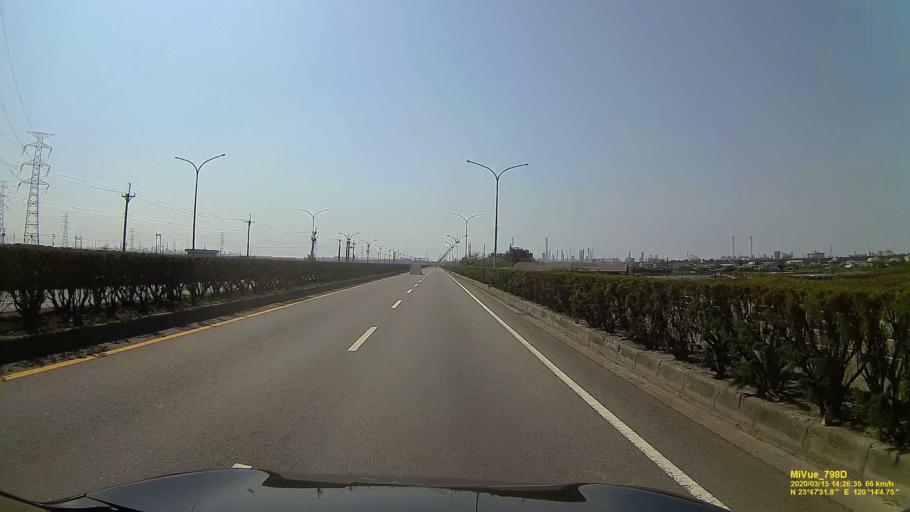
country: TW
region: Taiwan
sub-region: Yunlin
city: Douliu
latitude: 23.7922
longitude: 120.2343
